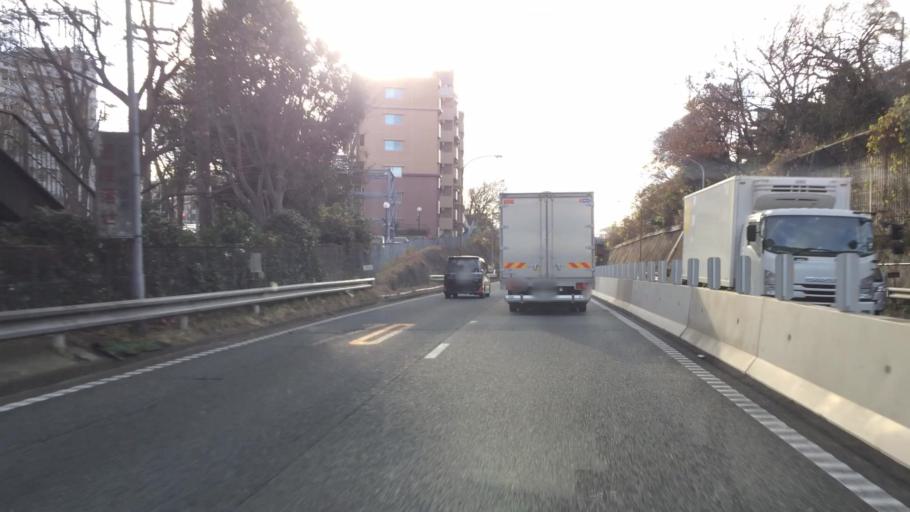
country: JP
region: Kanagawa
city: Yokohama
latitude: 35.4283
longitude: 139.5466
